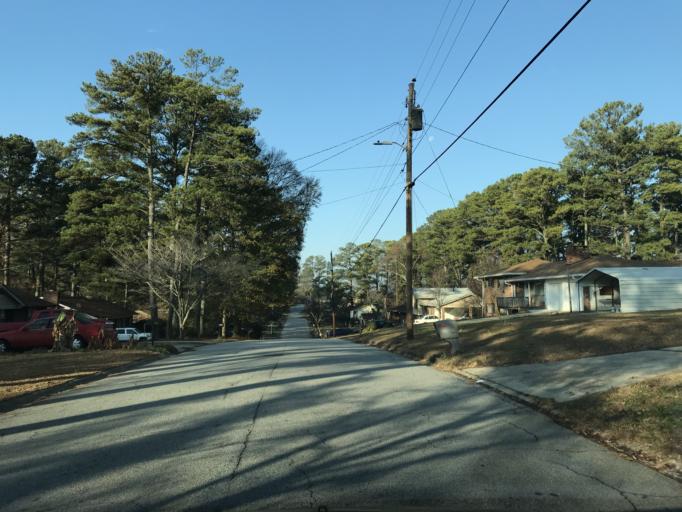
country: US
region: Georgia
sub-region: Fulton County
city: College Park
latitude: 33.6155
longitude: -84.4321
